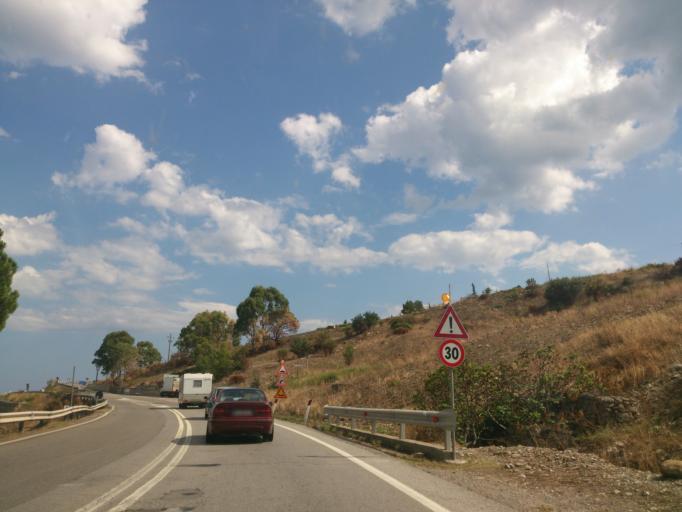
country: IT
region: Calabria
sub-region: Provincia di Cosenza
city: Roseto Capo Spulico
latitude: 39.9827
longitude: 16.6141
